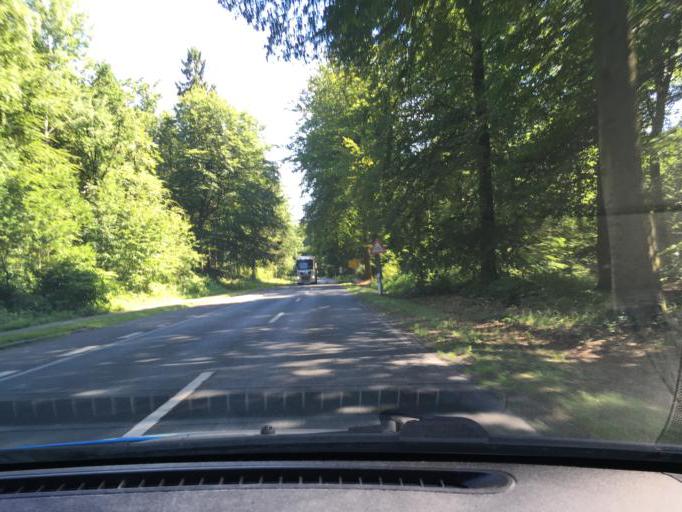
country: DE
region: Lower Saxony
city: Bendestorf
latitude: 53.3455
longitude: 9.9413
